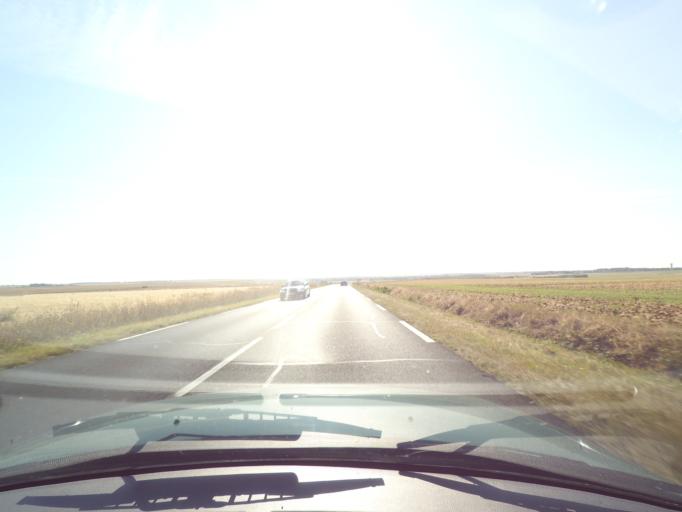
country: FR
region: Poitou-Charentes
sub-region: Departement de la Vienne
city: Cisse
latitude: 46.6308
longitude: 0.2460
